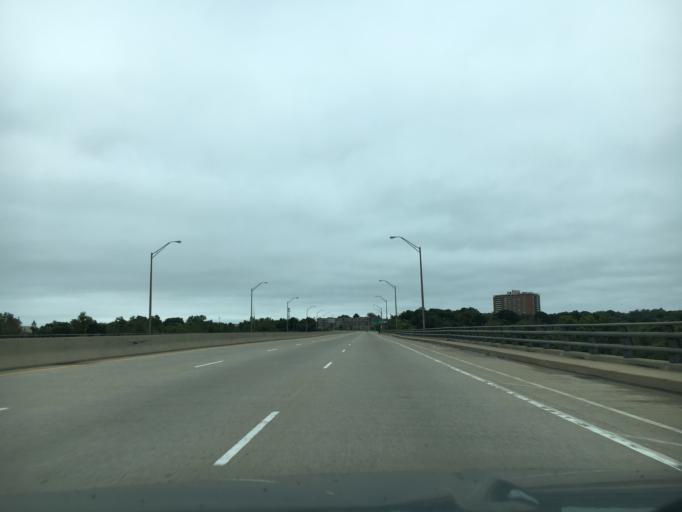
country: US
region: Virginia
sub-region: City of Richmond
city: Richmond
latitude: 37.5306
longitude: -77.4505
